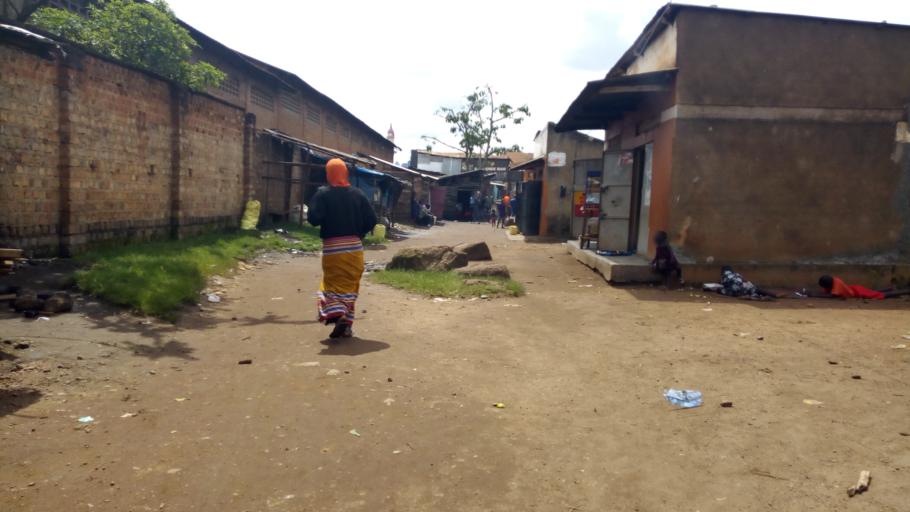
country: UG
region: Central Region
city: Kampala Central Division
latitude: 0.3564
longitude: 32.5618
